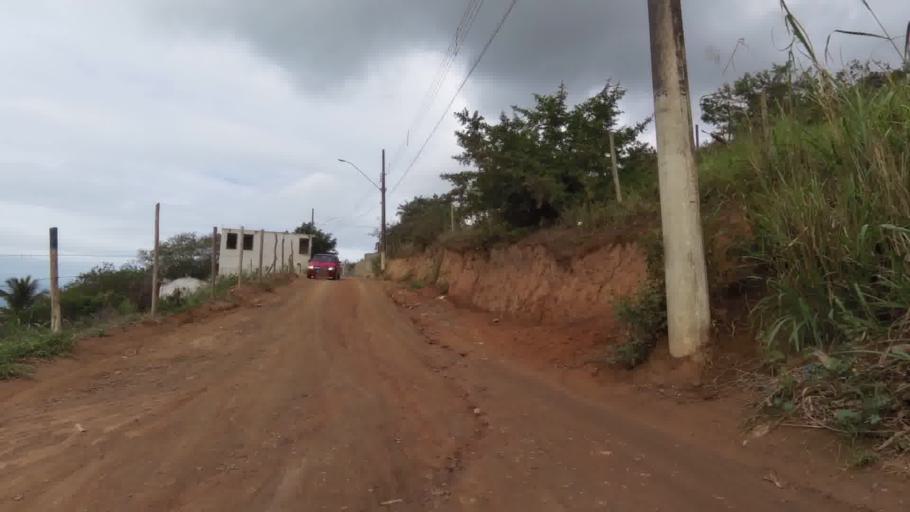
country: BR
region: Espirito Santo
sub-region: Marataizes
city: Marataizes
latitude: -21.0278
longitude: -40.8194
